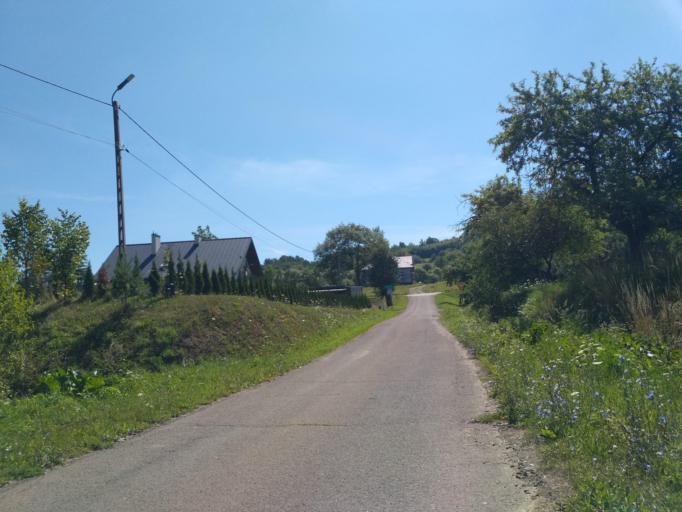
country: PL
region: Subcarpathian Voivodeship
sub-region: Powiat sanocki
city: Nowosielce-Gniewosz
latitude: 49.5274
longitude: 22.0440
